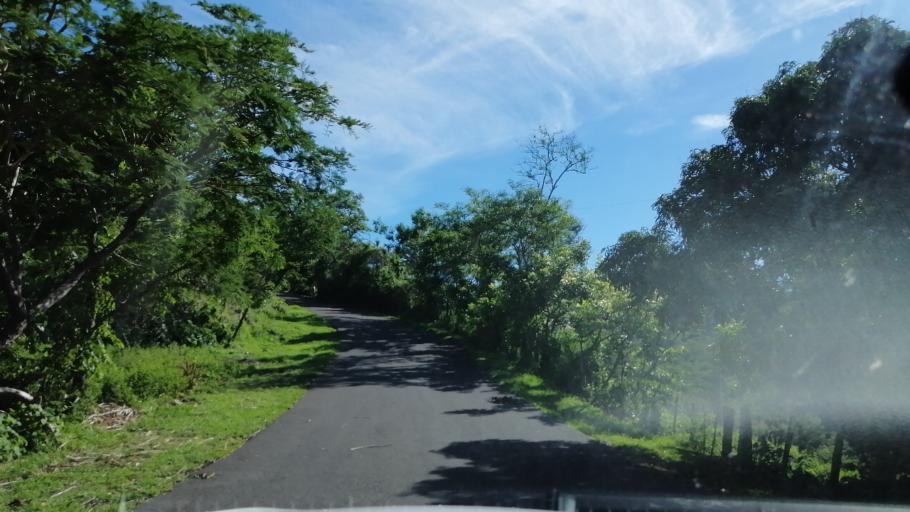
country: SV
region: Morazan
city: Corinto
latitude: 13.8059
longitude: -88.0035
